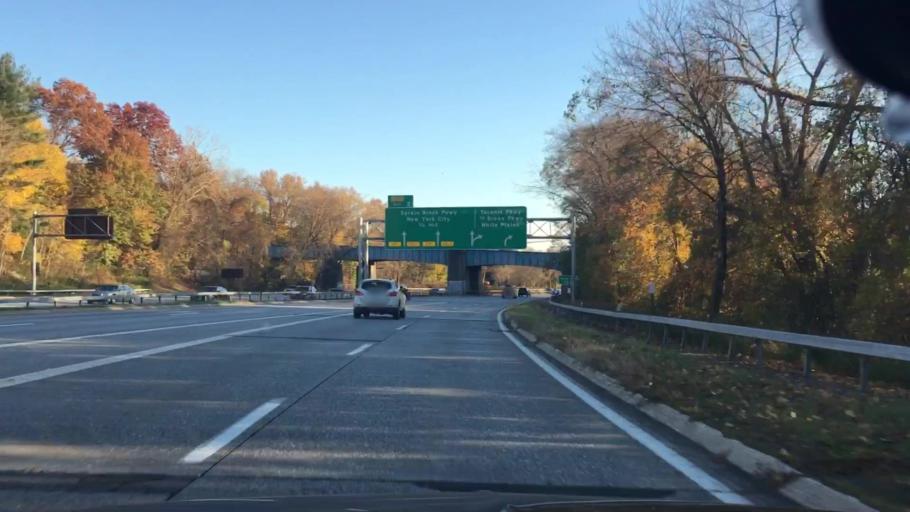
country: US
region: New York
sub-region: Westchester County
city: Hawthorne
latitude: 41.1056
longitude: -73.7977
